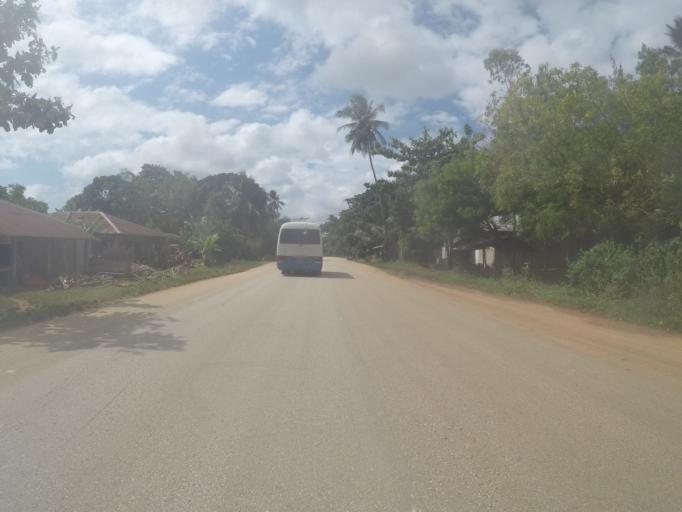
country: TZ
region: Zanzibar North
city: Mkokotoni
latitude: -5.8674
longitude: 39.2807
